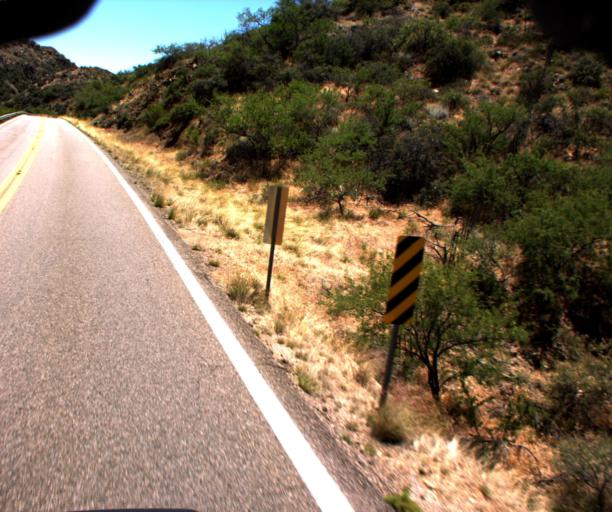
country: US
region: Arizona
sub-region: Gila County
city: Globe
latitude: 33.2126
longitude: -110.7977
